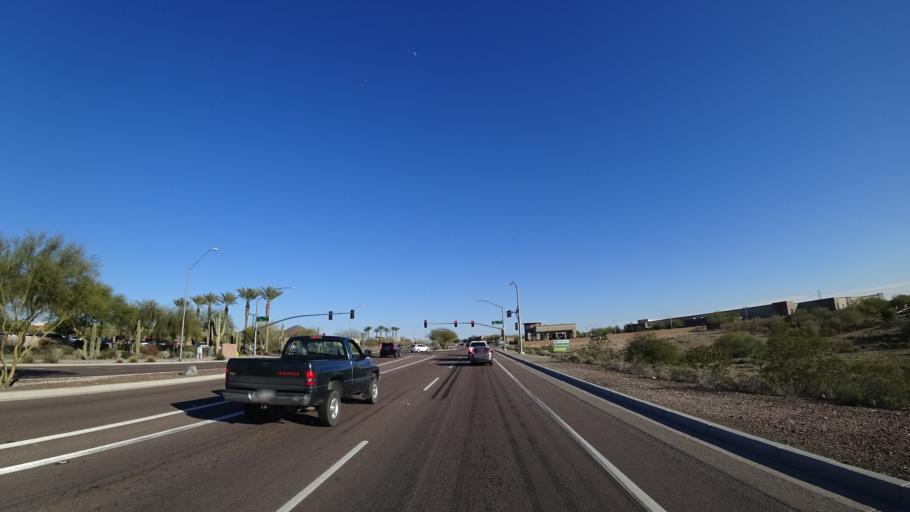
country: US
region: Arizona
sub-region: Maricopa County
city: Sun City West
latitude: 33.7121
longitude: -112.2772
